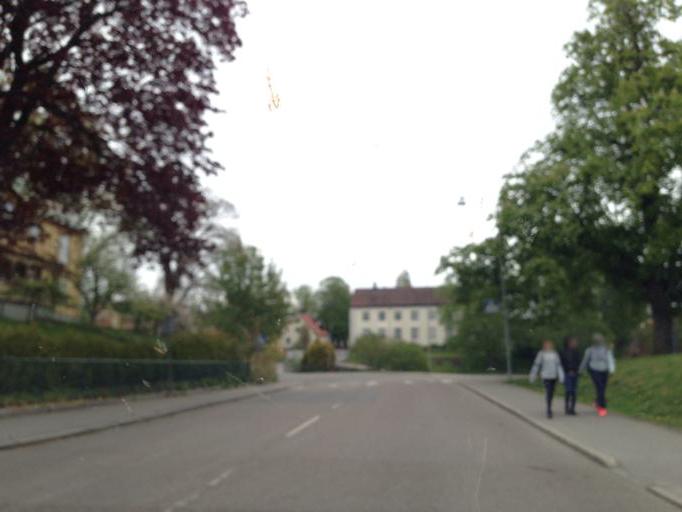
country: SE
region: Soedermanland
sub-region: Nykopings Kommun
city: Nykoping
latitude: 58.7495
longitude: 17.0092
